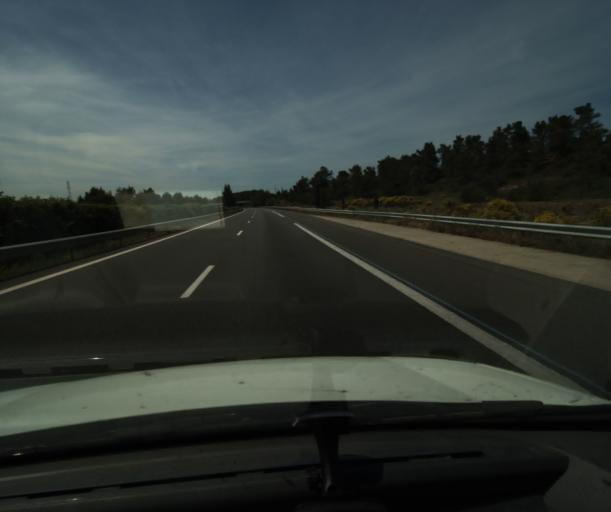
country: FR
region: Languedoc-Roussillon
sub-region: Departement de l'Aude
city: Palaja
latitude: 43.1892
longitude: 2.3826
